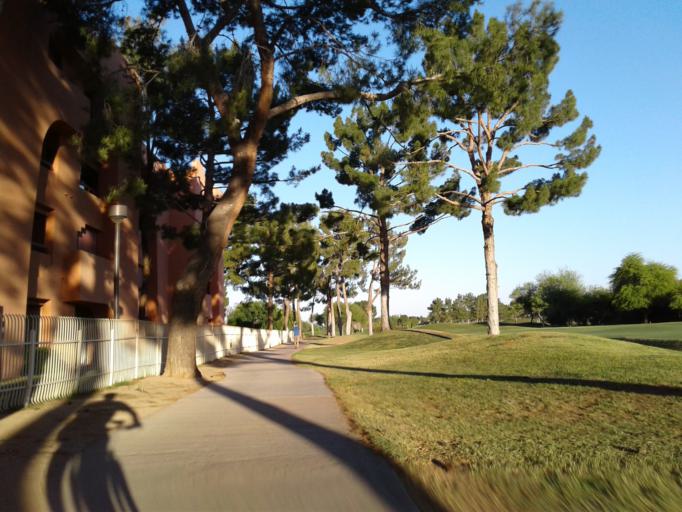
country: US
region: Arizona
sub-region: Maricopa County
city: Paradise Valley
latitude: 33.5962
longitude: -111.9887
